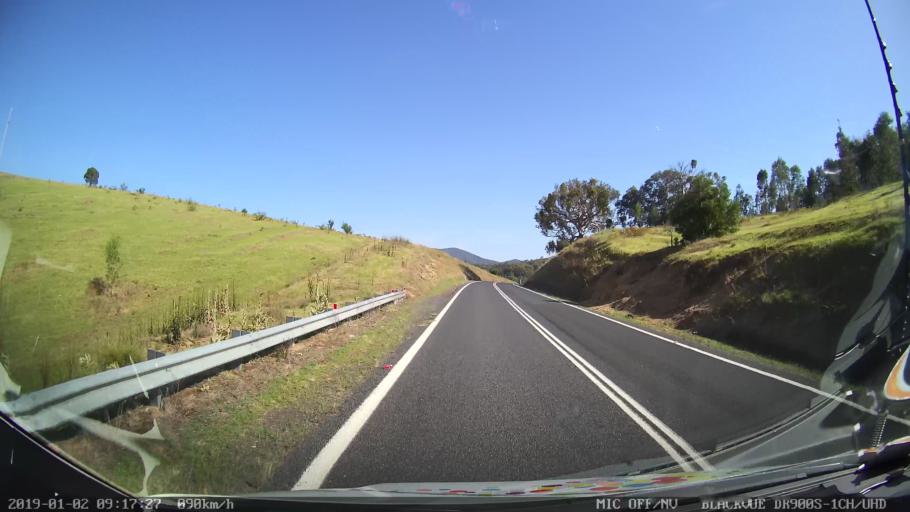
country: AU
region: New South Wales
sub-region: Tumut Shire
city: Tumut
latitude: -35.4402
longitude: 148.2867
